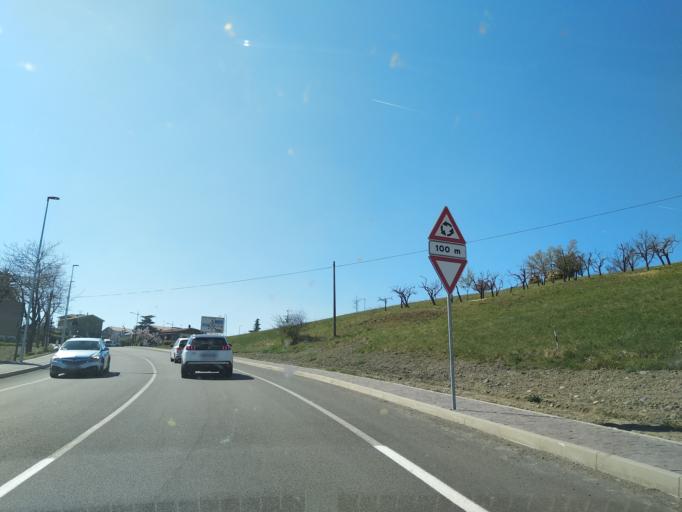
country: IT
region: Emilia-Romagna
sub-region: Provincia di Reggio Emilia
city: Castelnovo ne'Monti
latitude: 44.4332
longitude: 10.4120
